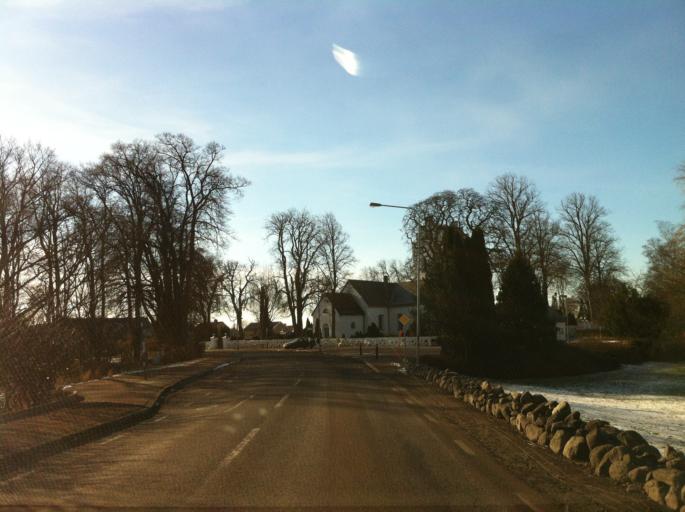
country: SE
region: Skane
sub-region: Angelholms Kommun
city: Strovelstorp
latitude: 56.1057
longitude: 12.7981
